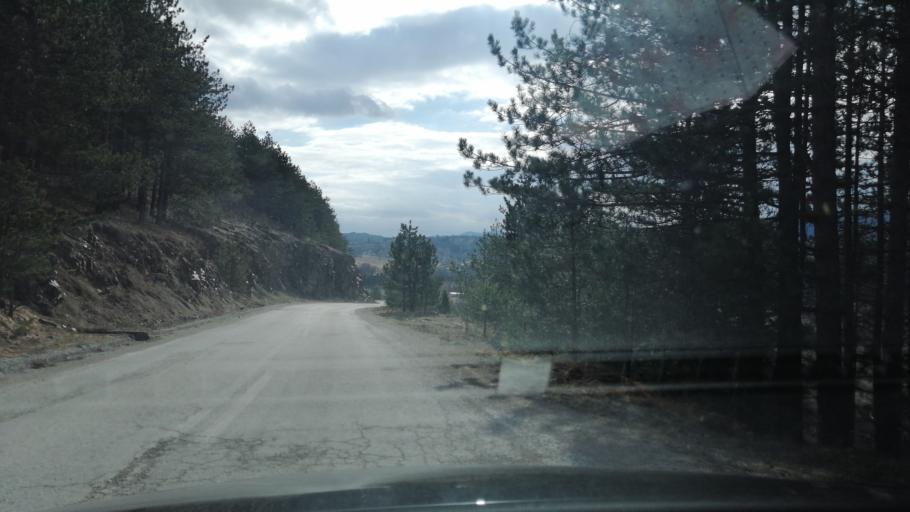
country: RS
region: Central Serbia
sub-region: Zlatiborski Okrug
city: Bajina Basta
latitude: 43.8619
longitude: 19.5778
